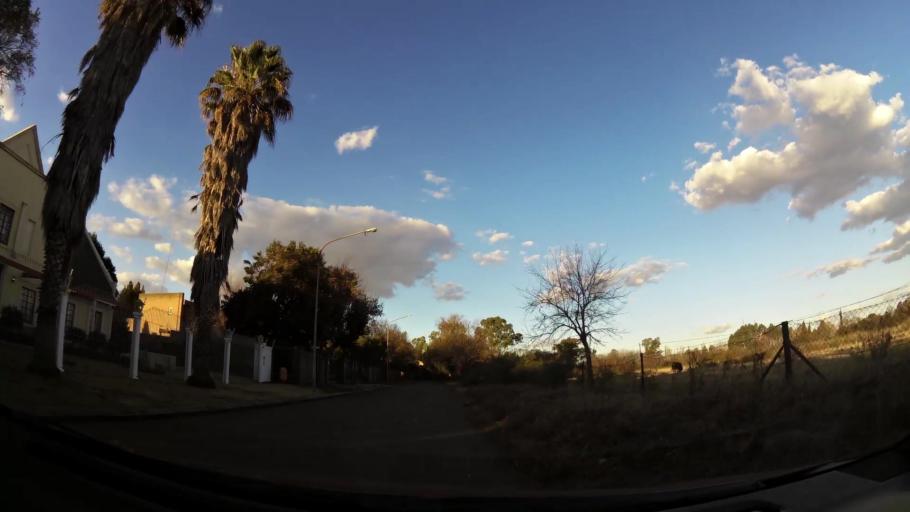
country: ZA
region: North-West
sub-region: Dr Kenneth Kaunda District Municipality
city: Potchefstroom
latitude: -26.6806
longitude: 27.1072
